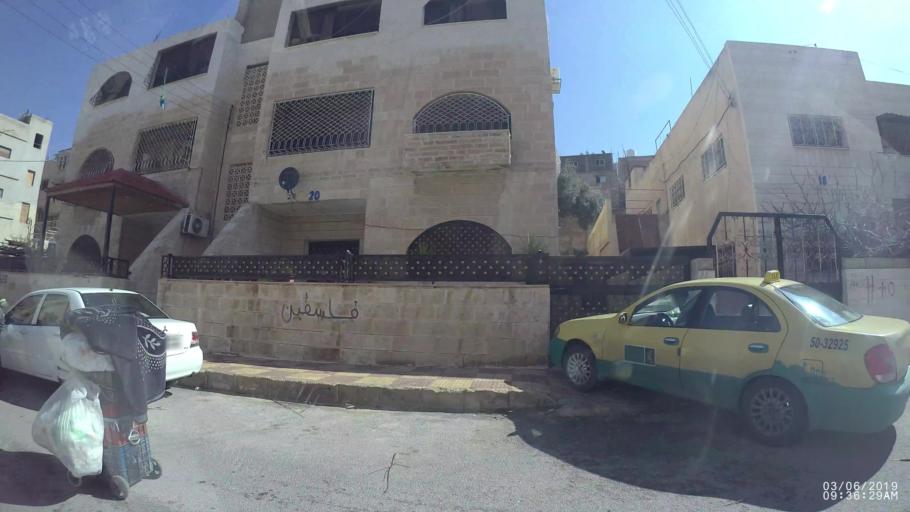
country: JO
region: Amman
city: Amman
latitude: 31.9879
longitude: 35.9841
